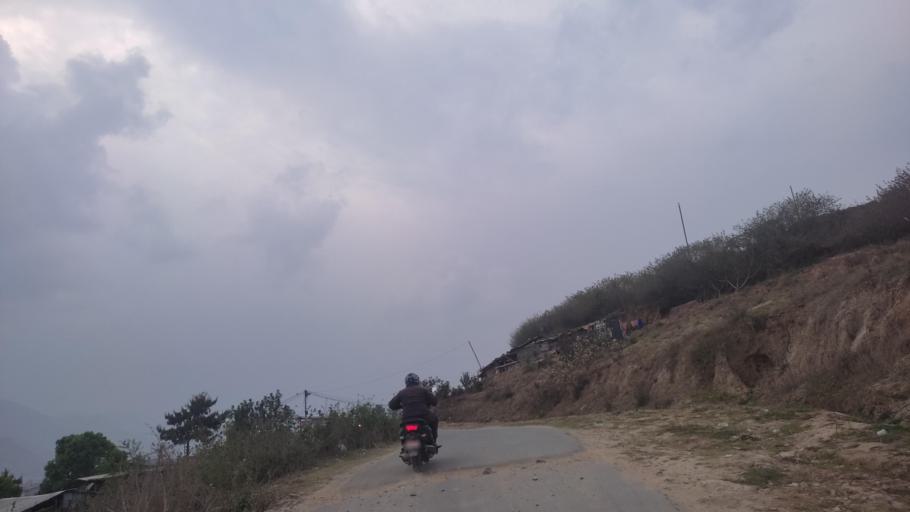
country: NP
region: Central Region
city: Kirtipur
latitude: 27.6618
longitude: 85.2895
